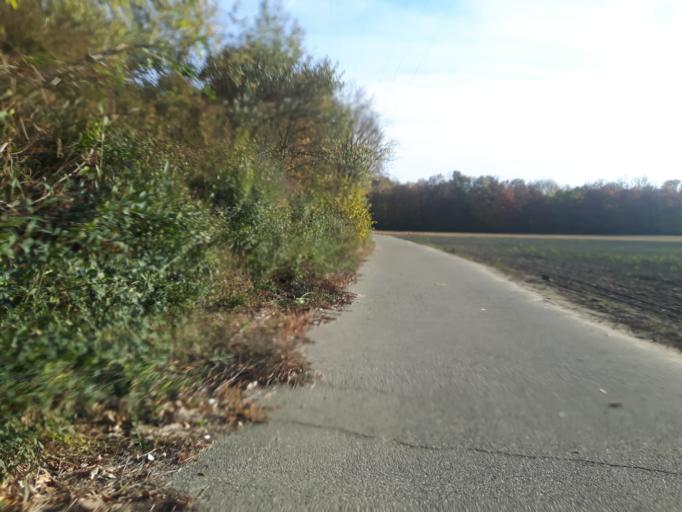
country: DE
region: Rheinland-Pfalz
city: Frankenthal
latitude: 49.5269
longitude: 8.4059
